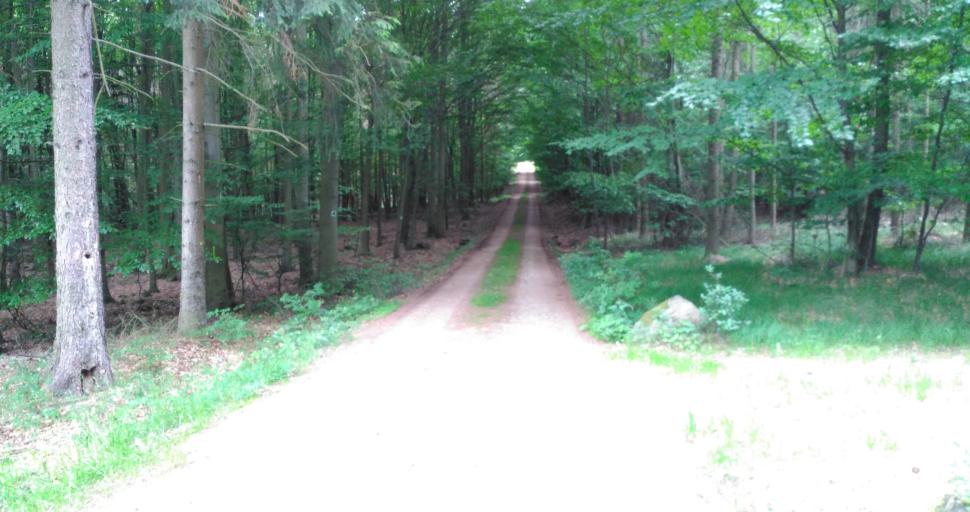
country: CZ
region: Central Bohemia
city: Zebrak
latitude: 49.9217
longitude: 13.8516
